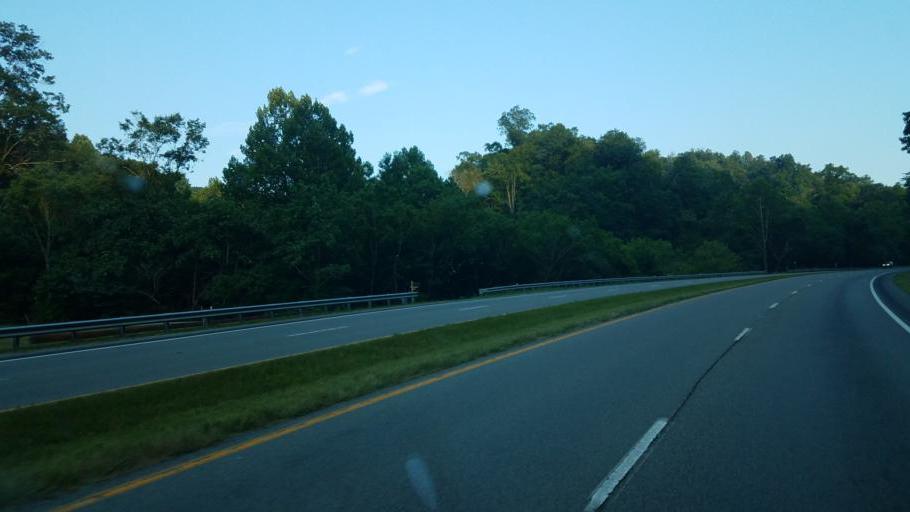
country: US
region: Virginia
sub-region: Wise County
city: Big Stone Gap
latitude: 36.7091
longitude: -82.7780
